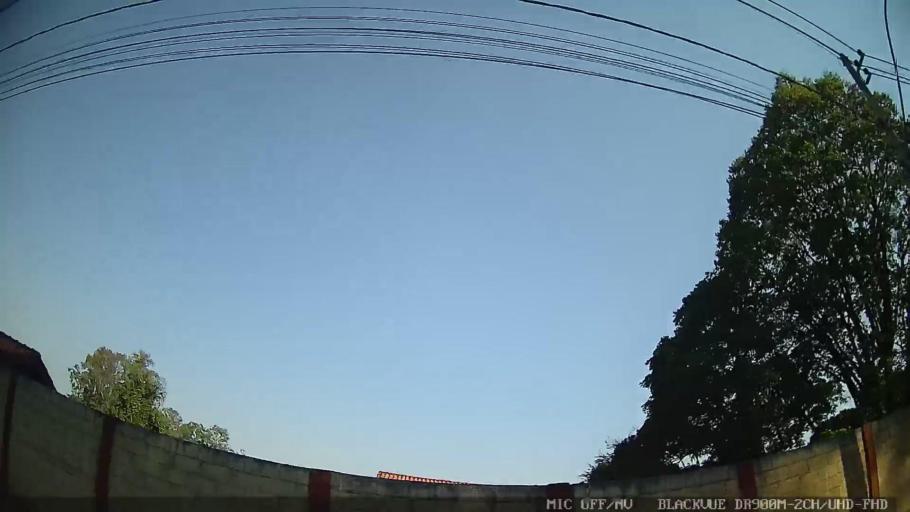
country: BR
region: Sao Paulo
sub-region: Itatiba
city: Itatiba
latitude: -22.9860
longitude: -46.8308
